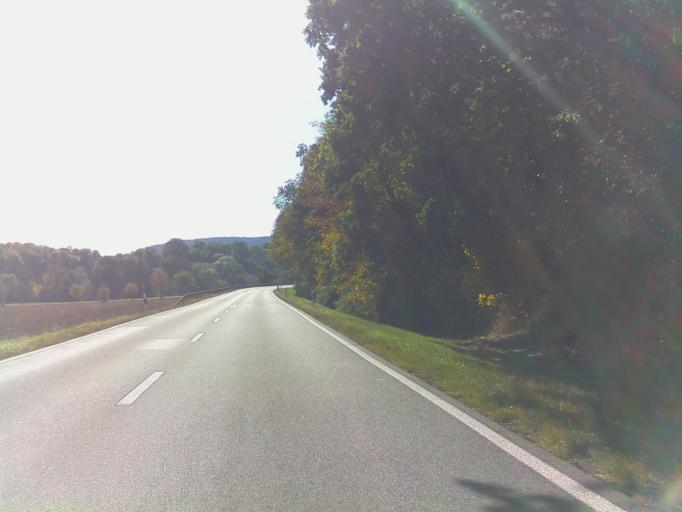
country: DE
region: Thuringia
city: Barchfeld
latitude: 50.7996
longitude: 11.1614
